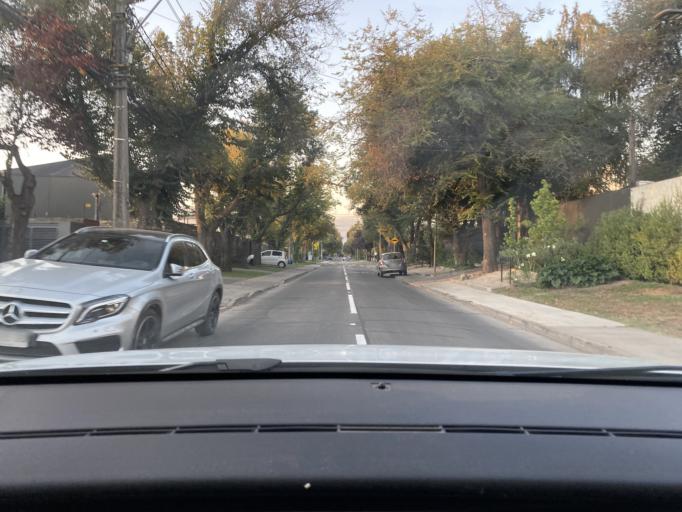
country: CL
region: Santiago Metropolitan
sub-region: Provincia de Santiago
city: Villa Presidente Frei, Nunoa, Santiago, Chile
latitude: -33.4002
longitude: -70.5228
